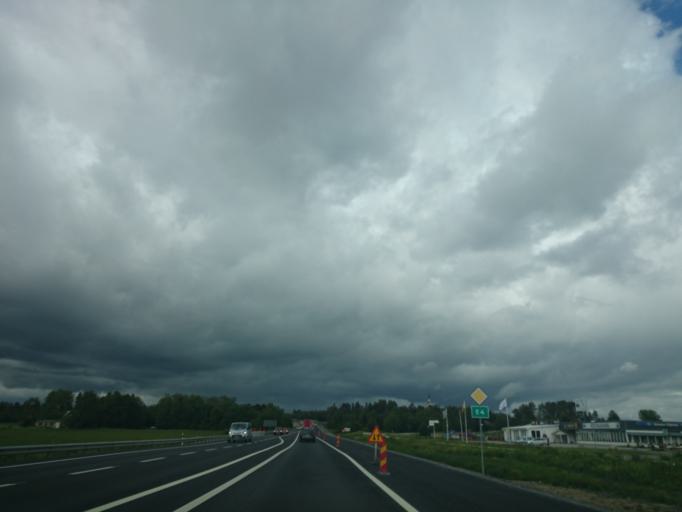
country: SE
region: Vaesternorrland
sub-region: Sundsvalls Kommun
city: Njurundabommen
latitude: 62.2478
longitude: 17.3725
